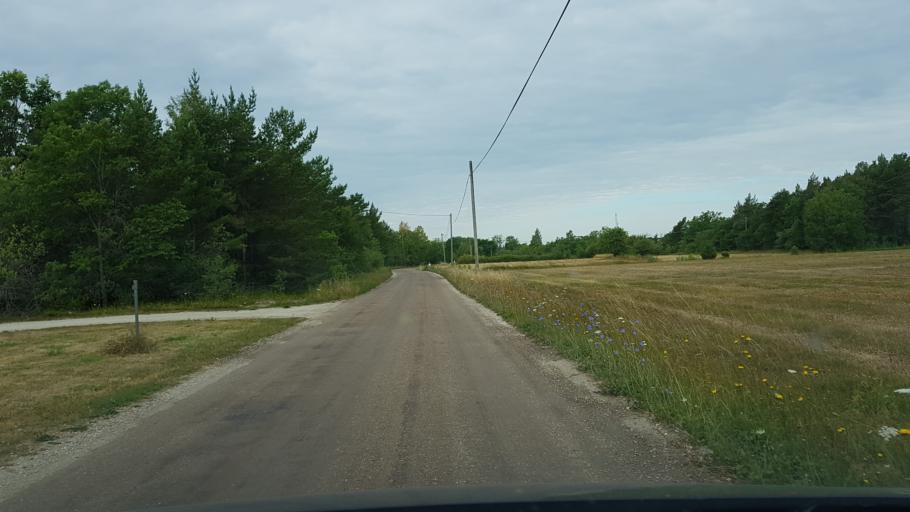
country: SE
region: Gotland
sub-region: Gotland
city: Visby
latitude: 57.8031
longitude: 18.5028
